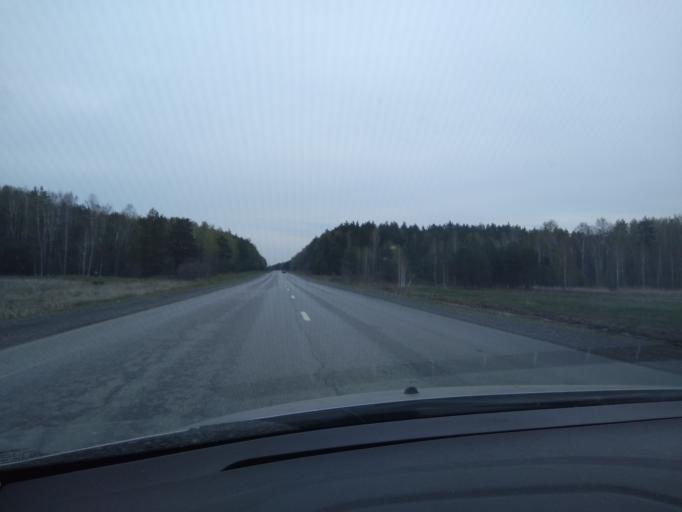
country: RU
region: Sverdlovsk
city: Baraba
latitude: 56.7832
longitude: 61.7687
